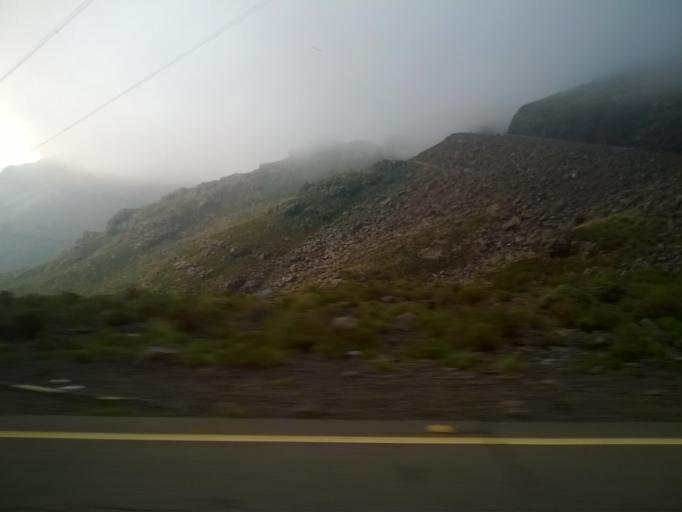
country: LS
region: Butha-Buthe
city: Butha-Buthe
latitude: -29.0640
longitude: 28.4019
